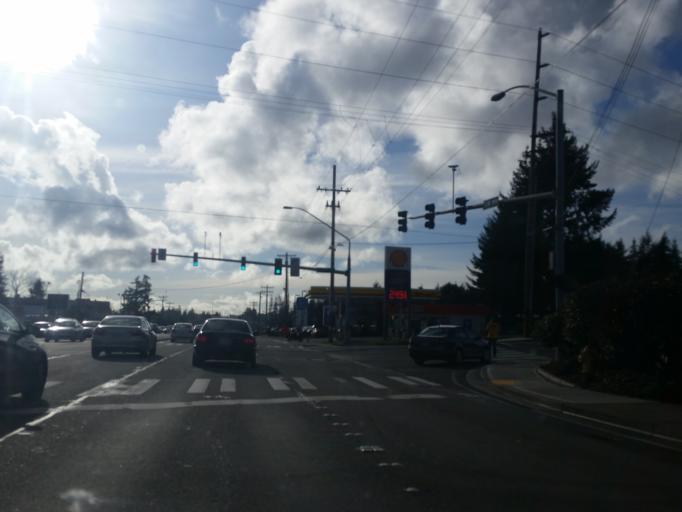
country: US
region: Washington
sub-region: Snohomish County
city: Mountlake Terrace
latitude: 47.8000
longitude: -122.3316
